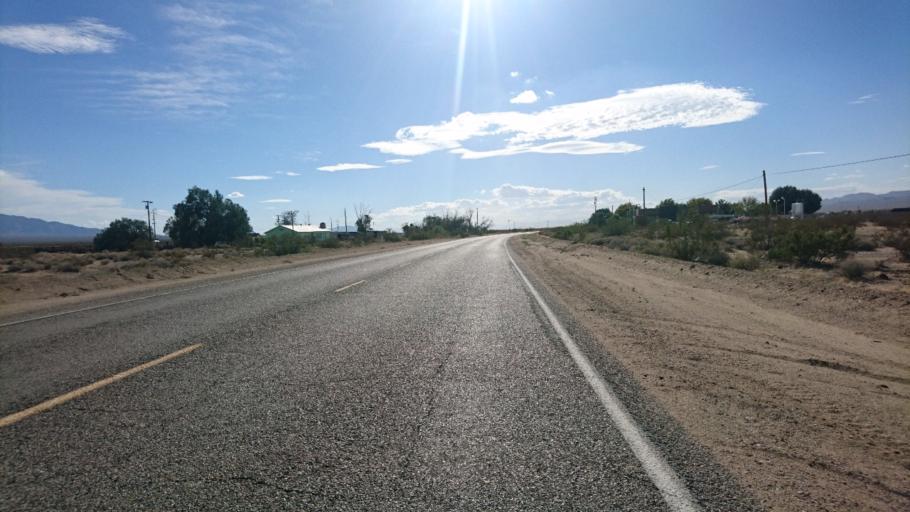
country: US
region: California
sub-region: San Bernardino County
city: Needles
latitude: 34.7331
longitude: -115.2478
